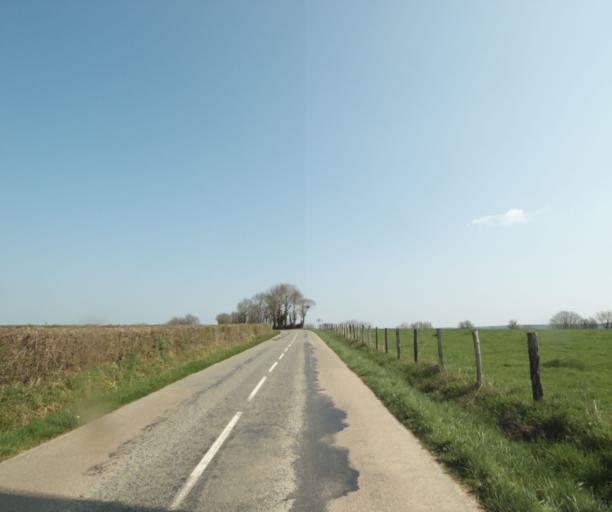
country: FR
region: Bourgogne
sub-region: Departement de Saone-et-Loire
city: Charolles
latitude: 46.4817
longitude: 4.3437
